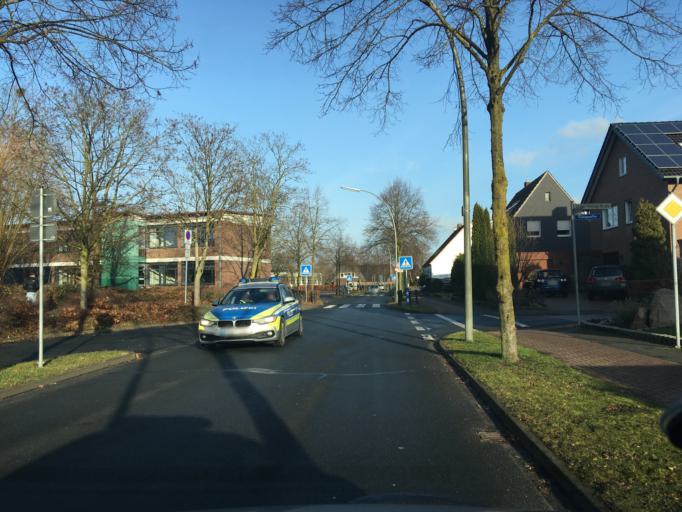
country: DE
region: North Rhine-Westphalia
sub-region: Regierungsbezirk Munster
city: Gescher
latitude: 51.9508
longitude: 6.9921
